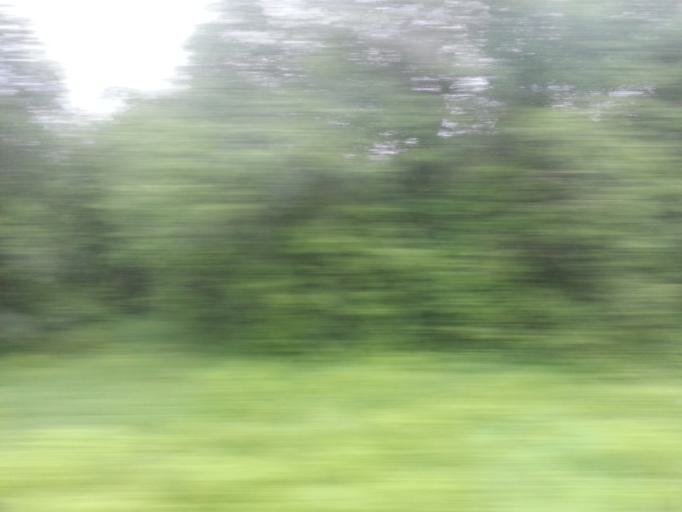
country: NO
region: Sor-Trondelag
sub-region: Melhus
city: Lundamo
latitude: 63.1047
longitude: 10.2281
